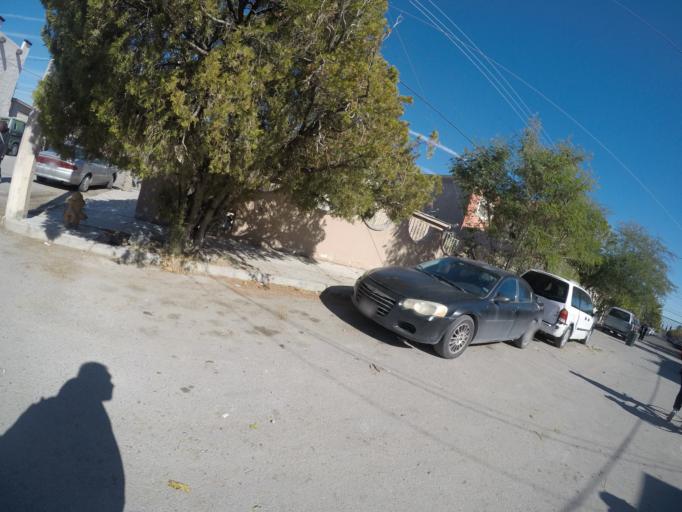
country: MX
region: Chihuahua
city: Ciudad Juarez
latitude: 31.7294
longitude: -106.4302
